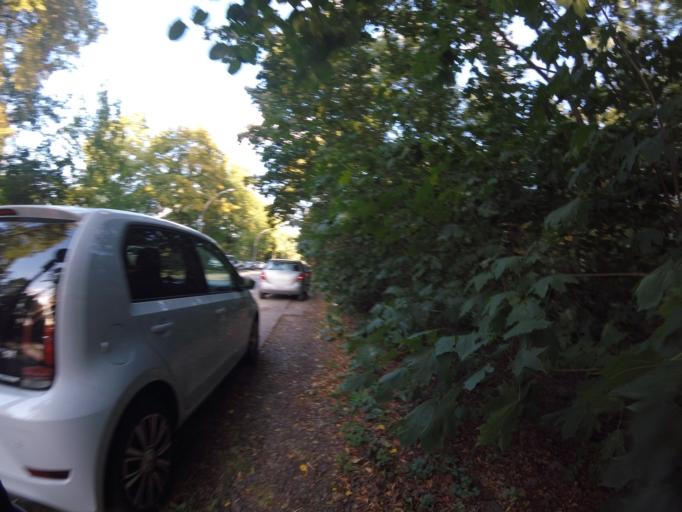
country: DE
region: Berlin
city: Charlottenburg-Nord
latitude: 52.5483
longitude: 13.2843
